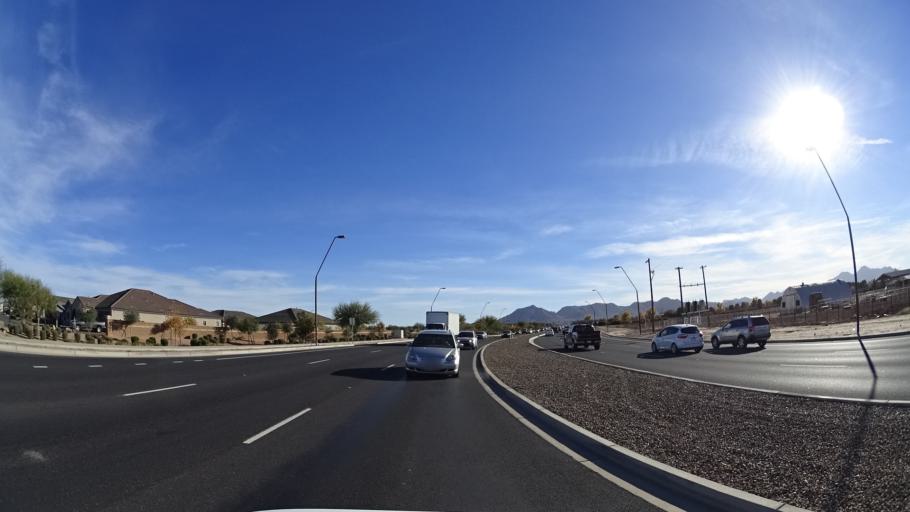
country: US
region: Arizona
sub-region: Maricopa County
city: Queen Creek
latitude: 33.2387
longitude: -111.6346
